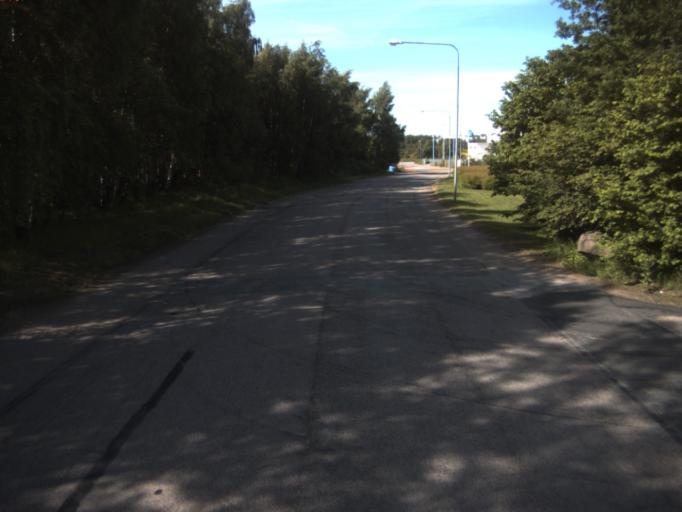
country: SE
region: Skane
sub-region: Helsingborg
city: Odakra
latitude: 56.0730
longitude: 12.7444
